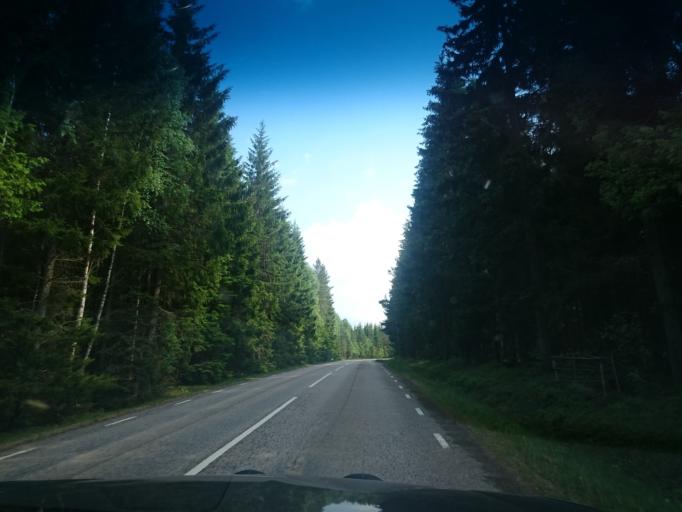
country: SE
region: Joenkoeping
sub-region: Vetlanda Kommun
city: Vetlanda
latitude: 57.3580
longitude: 15.0710
